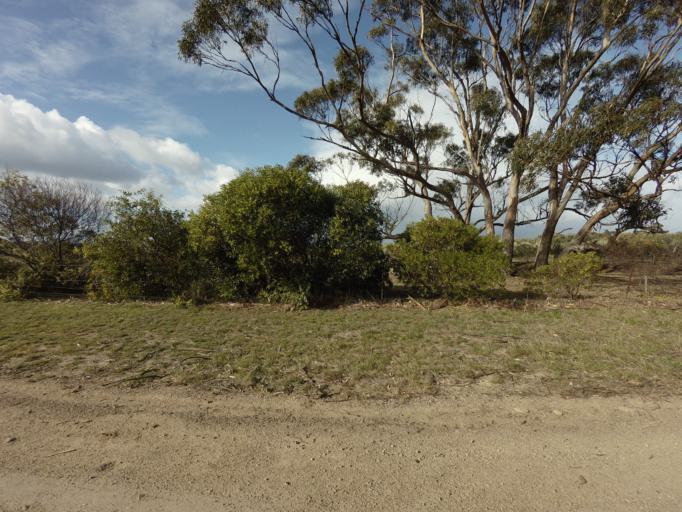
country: AU
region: Tasmania
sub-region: Sorell
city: Sorell
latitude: -42.3056
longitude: 147.9965
